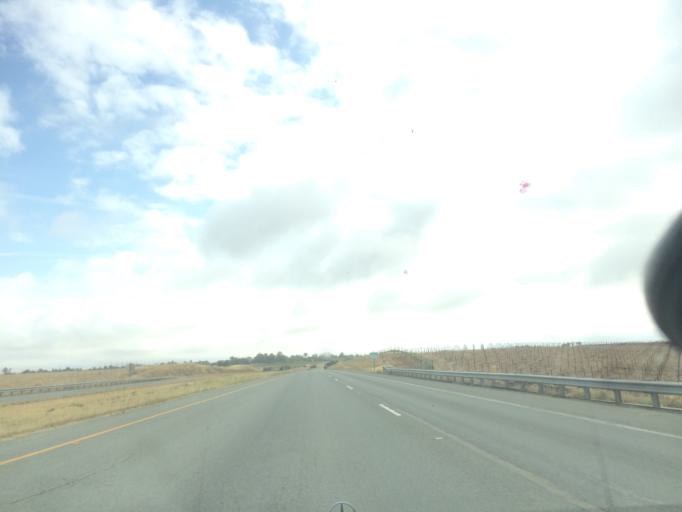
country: US
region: California
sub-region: San Luis Obispo County
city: Paso Robles
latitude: 35.6532
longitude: -120.6185
